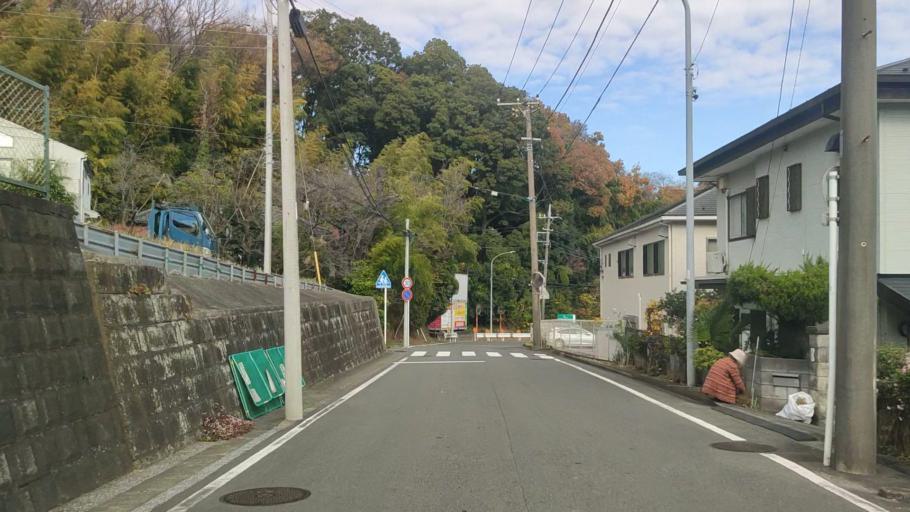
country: JP
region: Kanagawa
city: Yokohama
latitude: 35.4443
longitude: 139.5563
